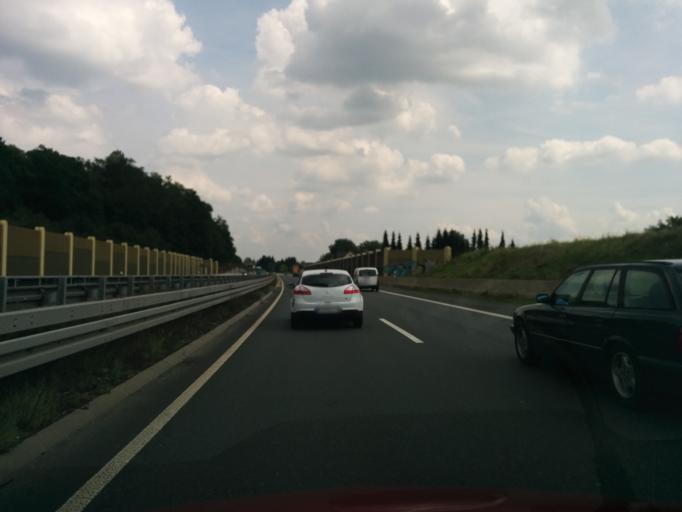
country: DE
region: Hesse
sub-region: Regierungsbezirk Giessen
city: Asslar
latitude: 50.5585
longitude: 8.4688
